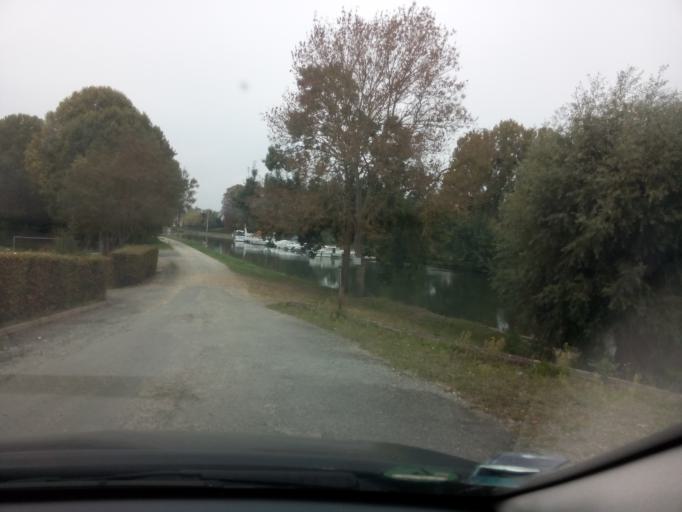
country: FR
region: Pays de la Loire
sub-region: Departement de Maine-et-Loire
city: Tierce
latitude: 47.6233
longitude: -0.5023
